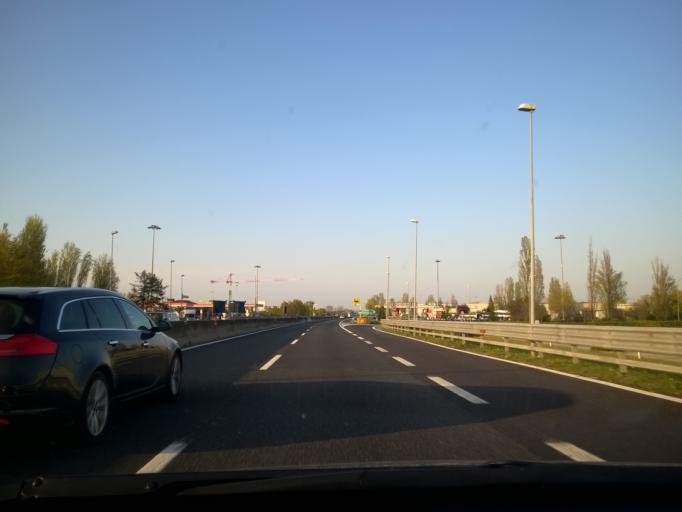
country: IT
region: Emilia-Romagna
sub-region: Provincia di Bologna
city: Bentivoglio
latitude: 44.6208
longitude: 11.4189
